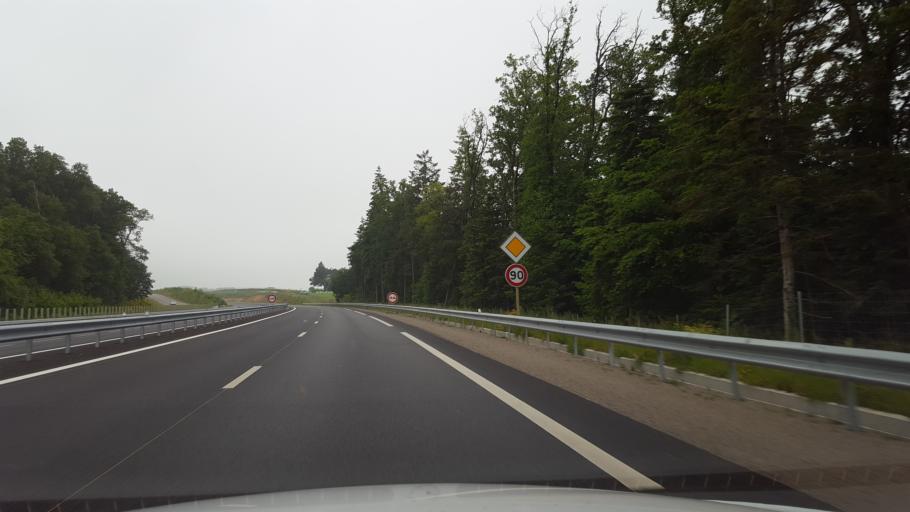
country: FR
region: Brittany
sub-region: Departement d'Ille-et-Vilaine
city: Guignen
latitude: 47.9170
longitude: -1.8577
